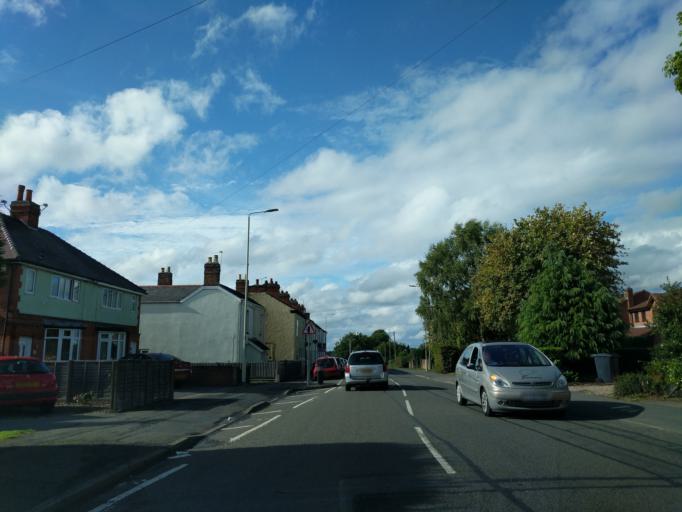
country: GB
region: England
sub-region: Leicestershire
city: Coalville
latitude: 52.7009
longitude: -1.3694
